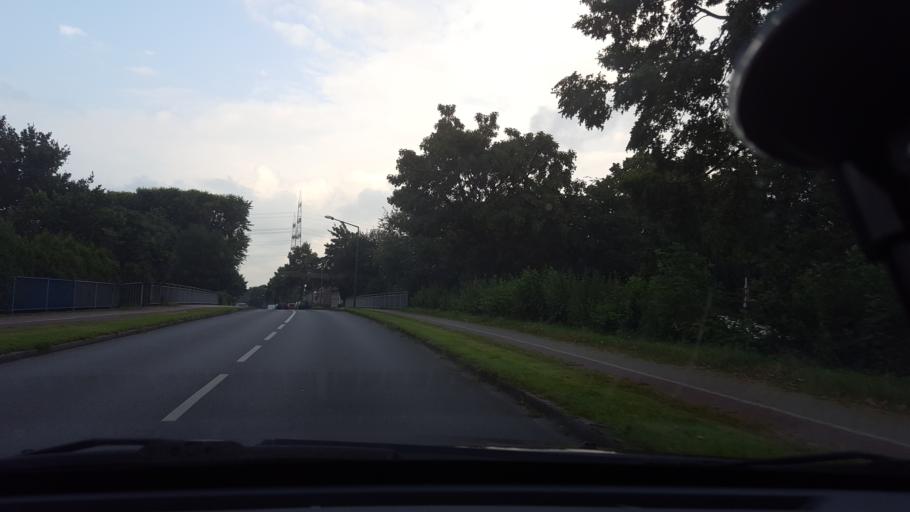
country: DE
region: North Rhine-Westphalia
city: Herten
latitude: 51.6025
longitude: 7.0979
